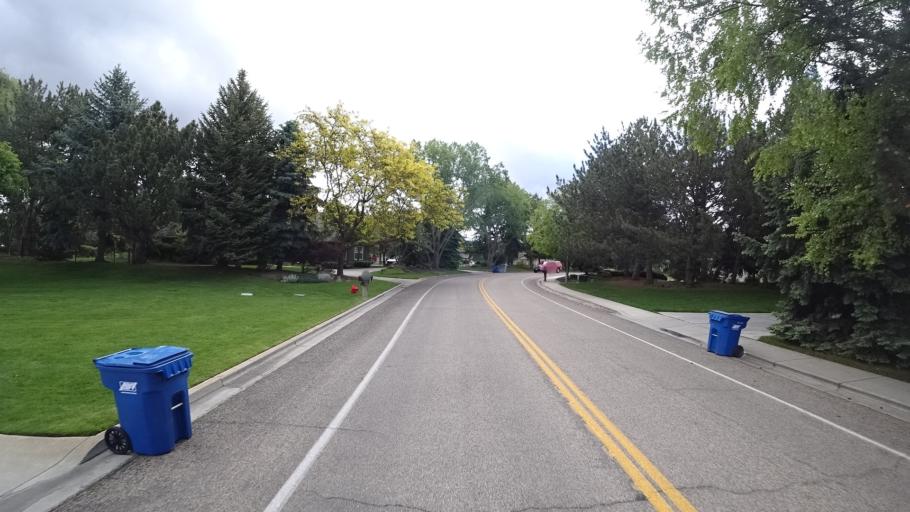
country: US
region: Idaho
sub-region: Ada County
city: Eagle
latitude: 43.6722
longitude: -116.2976
